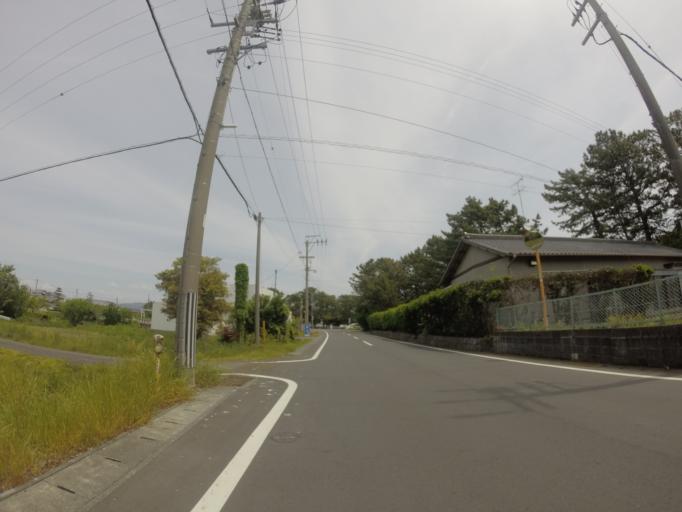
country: JP
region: Shizuoka
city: Yaizu
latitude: 34.8057
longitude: 138.3170
